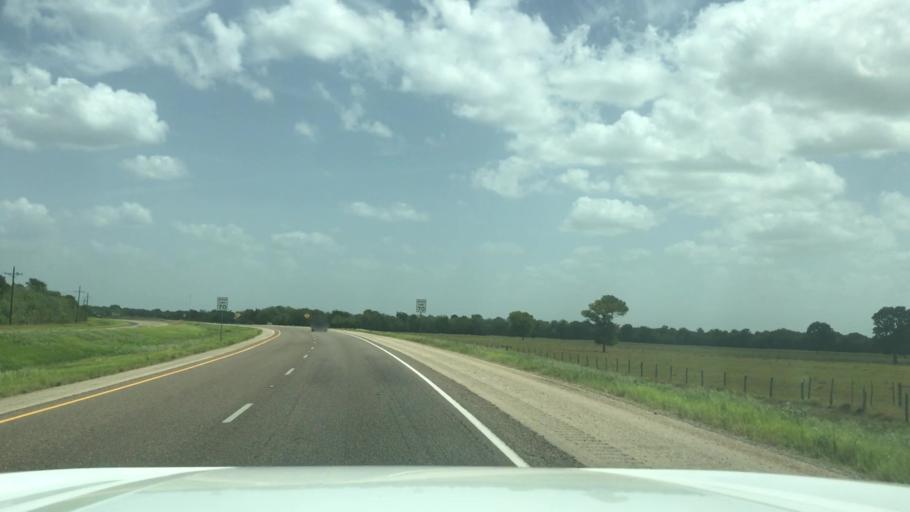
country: US
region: Texas
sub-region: Robertson County
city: Calvert
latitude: 30.9958
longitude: -96.6914
